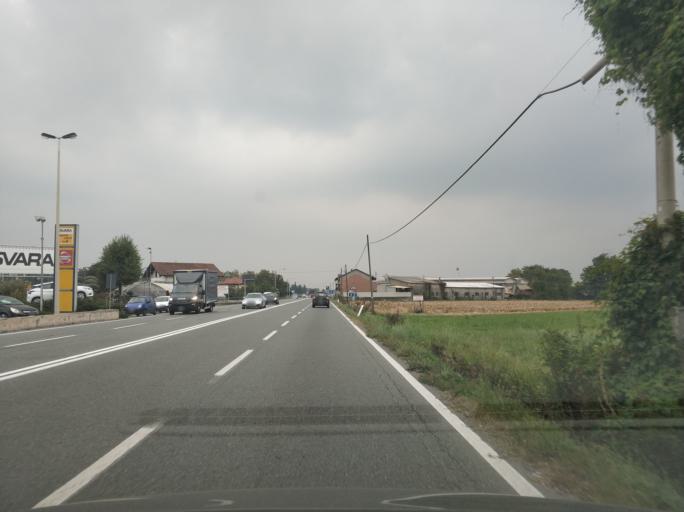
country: IT
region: Piedmont
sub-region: Provincia di Torino
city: Cirie
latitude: 45.2199
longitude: 7.6094
